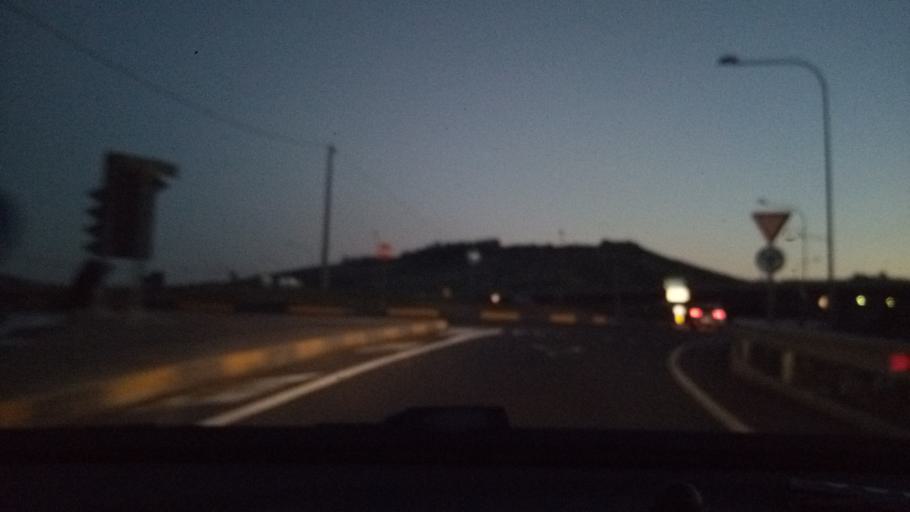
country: IT
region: Calabria
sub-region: Provincia di Catanzaro
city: Barone
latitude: 38.8633
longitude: 16.6333
